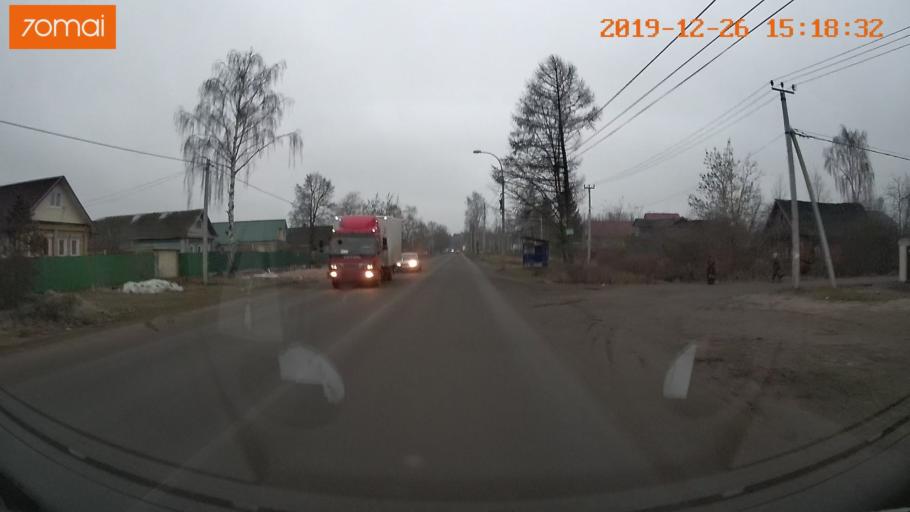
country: RU
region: Jaroslavl
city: Rybinsk
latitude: 58.0692
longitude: 38.8445
